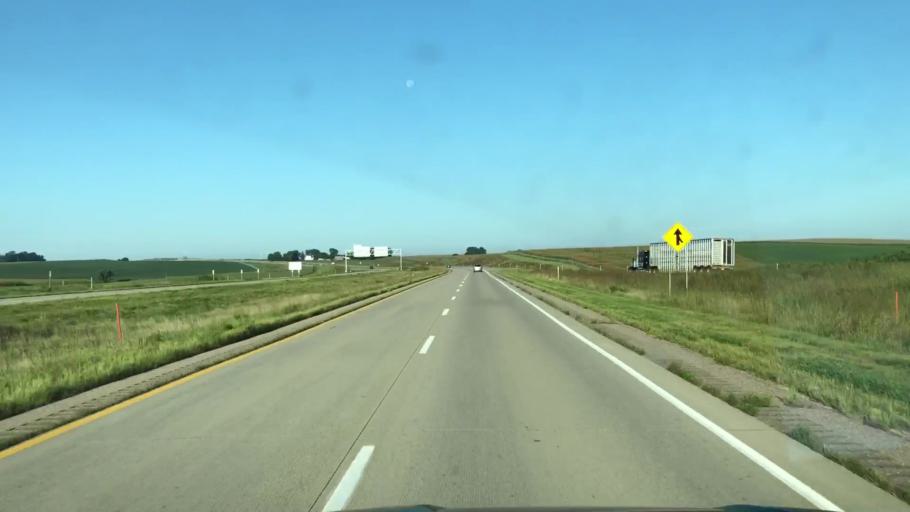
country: US
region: Iowa
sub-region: Plymouth County
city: Le Mars
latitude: 42.8180
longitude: -96.1776
